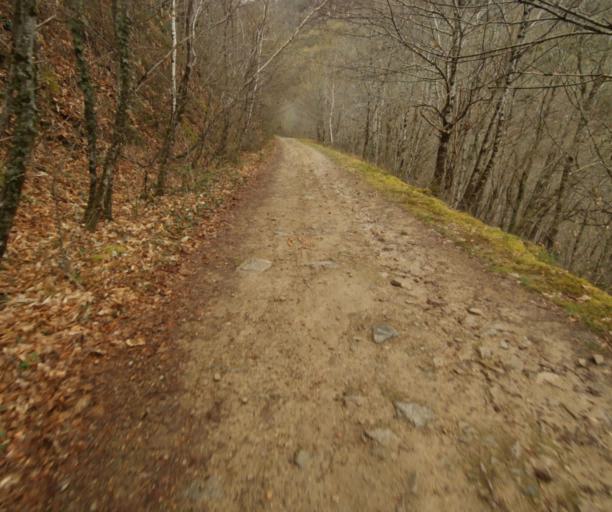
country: FR
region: Limousin
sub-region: Departement de la Correze
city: Saint-Privat
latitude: 45.2180
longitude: 2.0336
